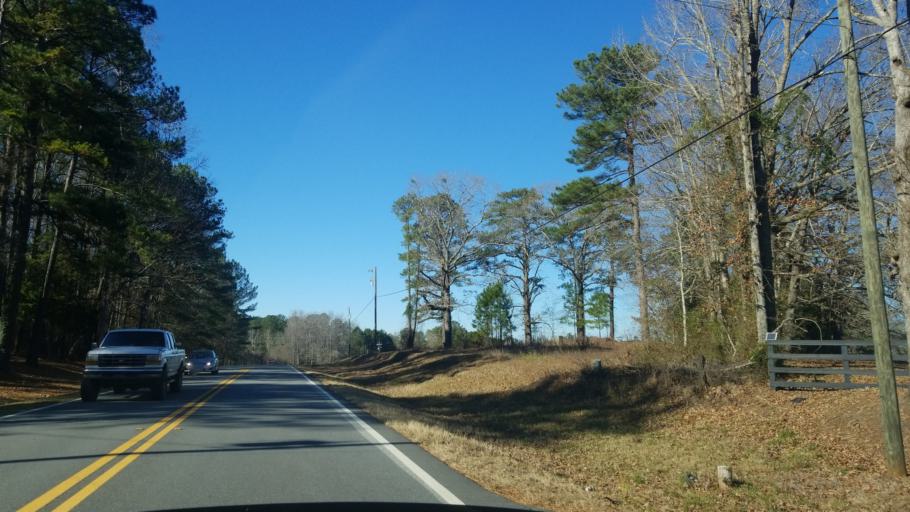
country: US
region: Georgia
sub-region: Harris County
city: Hamilton
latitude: 32.6719
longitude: -84.9054
